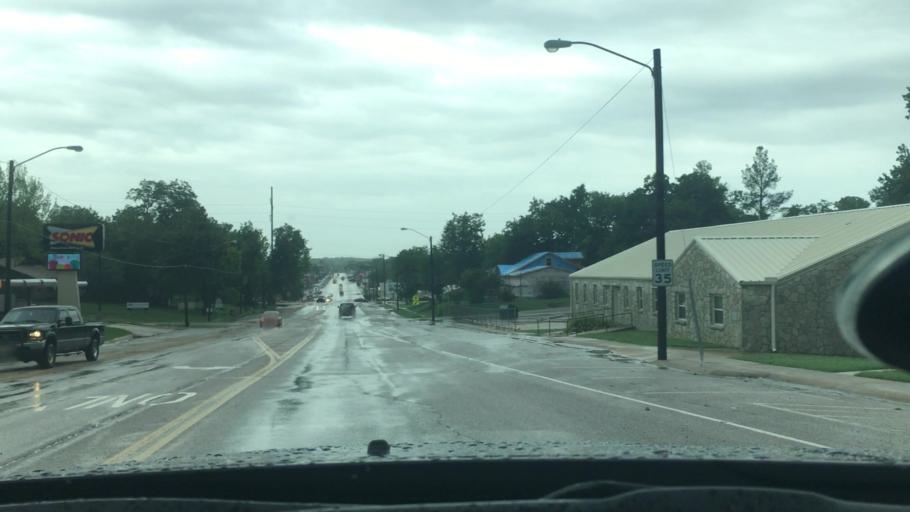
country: US
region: Oklahoma
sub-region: Johnston County
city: Tishomingo
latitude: 34.2324
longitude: -96.6732
